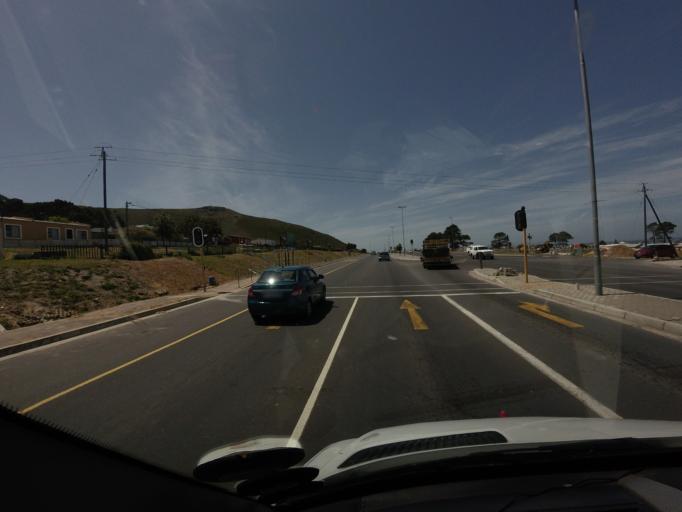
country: ZA
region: Western Cape
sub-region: Overberg District Municipality
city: Hermanus
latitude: -34.4144
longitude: 19.2087
